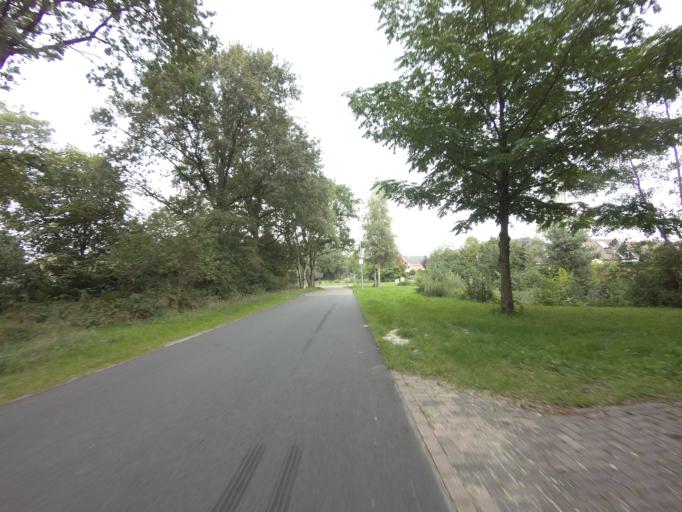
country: NL
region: Drenthe
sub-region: Gemeente Tynaarlo
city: Vries
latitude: 53.0668
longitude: 6.5810
